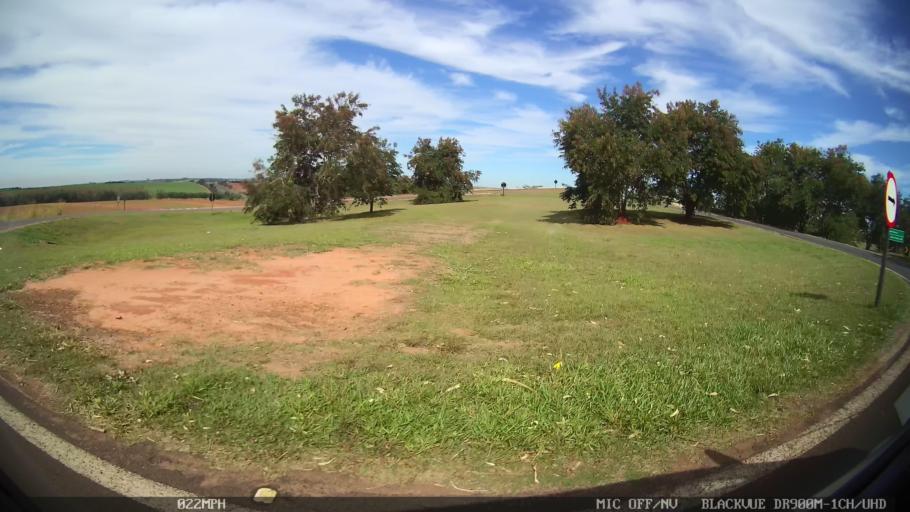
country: BR
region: Sao Paulo
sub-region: Taquaritinga
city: Taquaritinga
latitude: -21.4135
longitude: -48.6857
